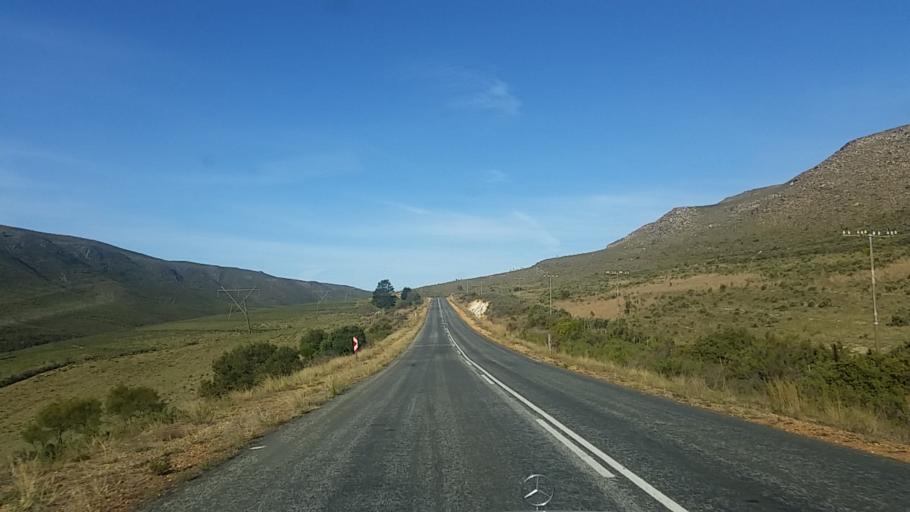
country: ZA
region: Western Cape
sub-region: Eden District Municipality
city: Knysna
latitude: -33.7442
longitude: 22.9935
